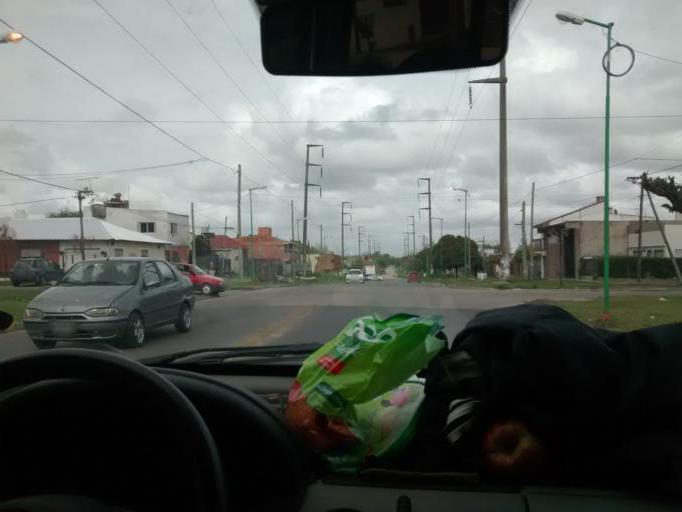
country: AR
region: Buenos Aires
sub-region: Partido de La Plata
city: La Plata
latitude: -34.9488
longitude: -57.9846
